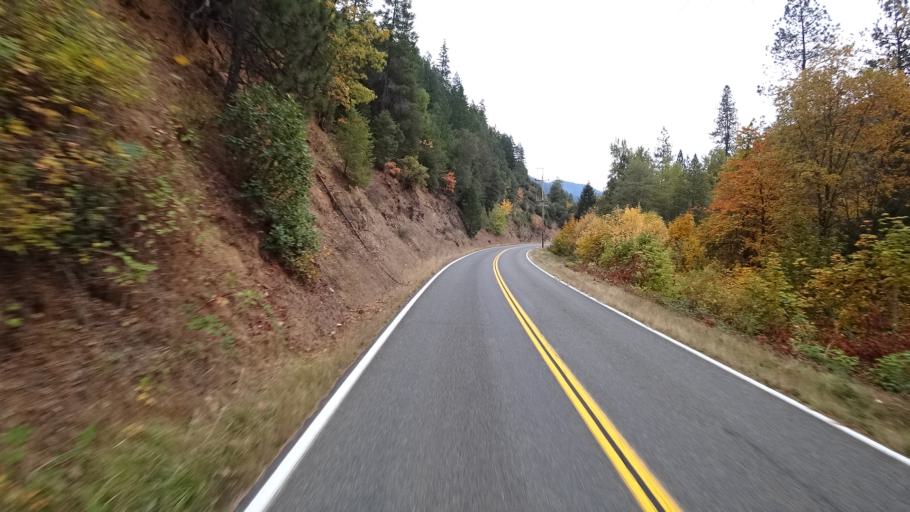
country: US
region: California
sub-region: Siskiyou County
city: Happy Camp
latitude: 41.8946
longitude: -123.4337
